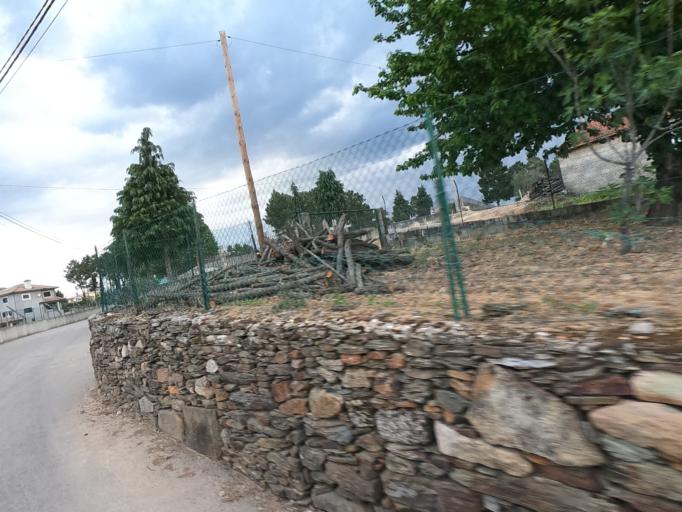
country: PT
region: Vila Real
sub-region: Vila Real
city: Vila Real
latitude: 41.2678
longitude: -7.6892
